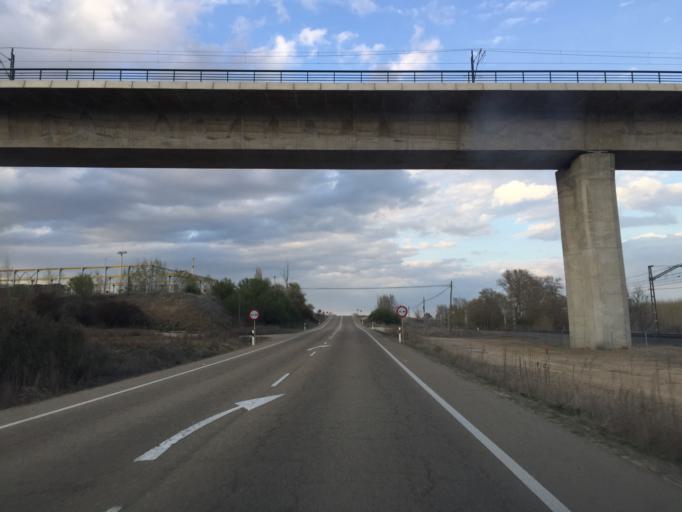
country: ES
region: Castille and Leon
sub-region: Provincia de Palencia
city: Soto de Cerrato
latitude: 41.9468
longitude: -4.4635
